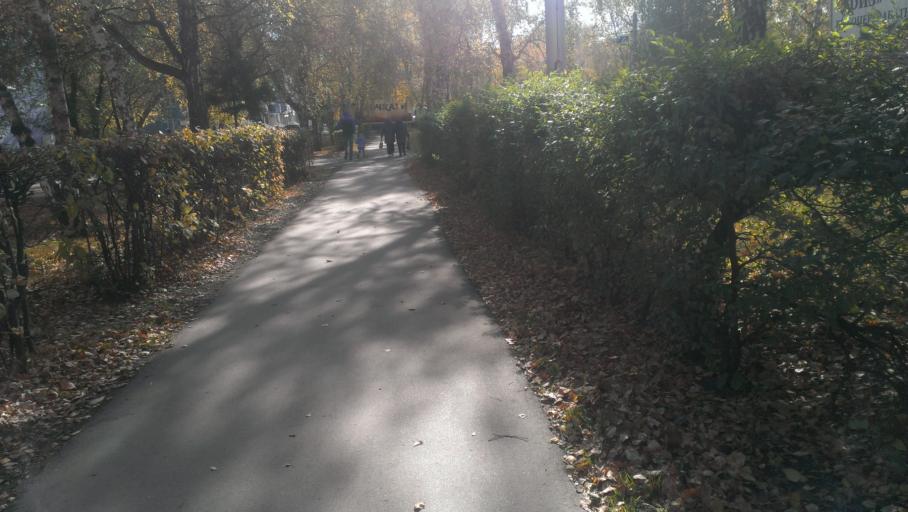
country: RU
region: Altai Krai
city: Novosilikatnyy
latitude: 53.3515
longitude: 83.6838
